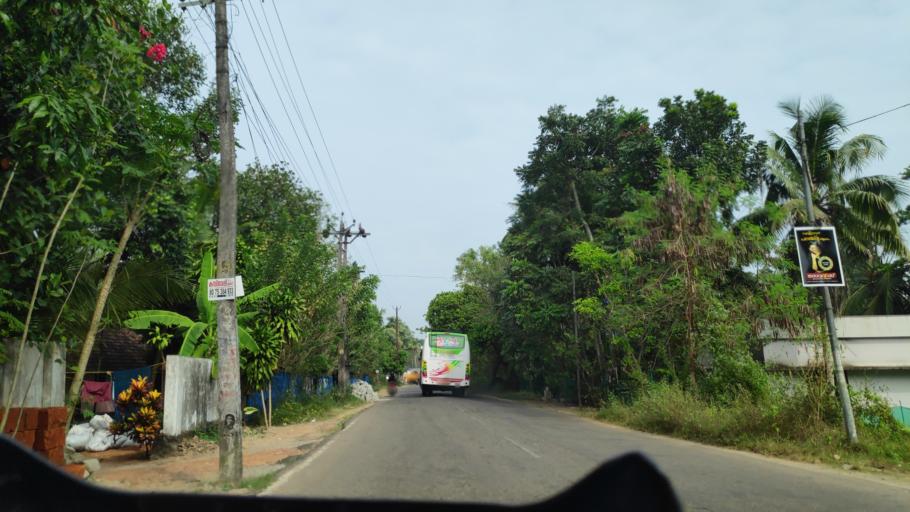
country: IN
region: Kerala
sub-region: Alappuzha
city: Kutiatodu
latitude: 9.8125
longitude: 76.3522
